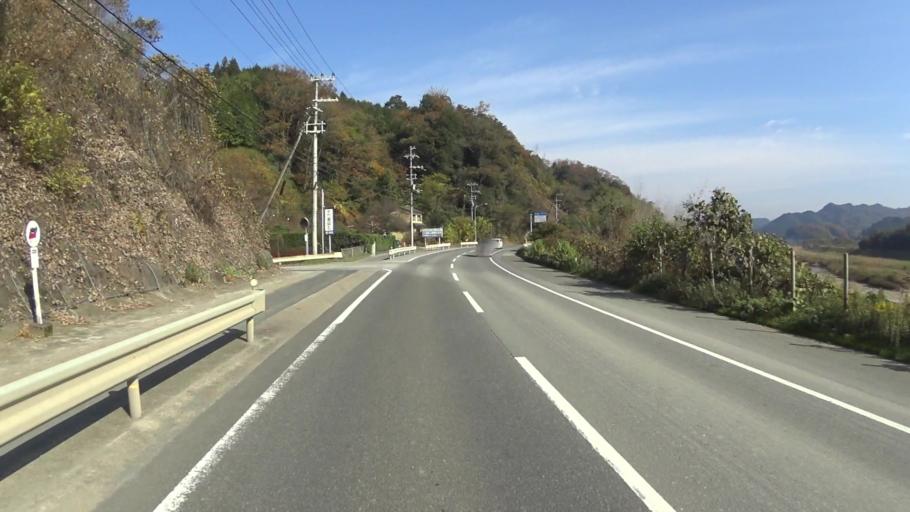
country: JP
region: Kyoto
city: Fukuchiyama
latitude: 35.3663
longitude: 135.1167
